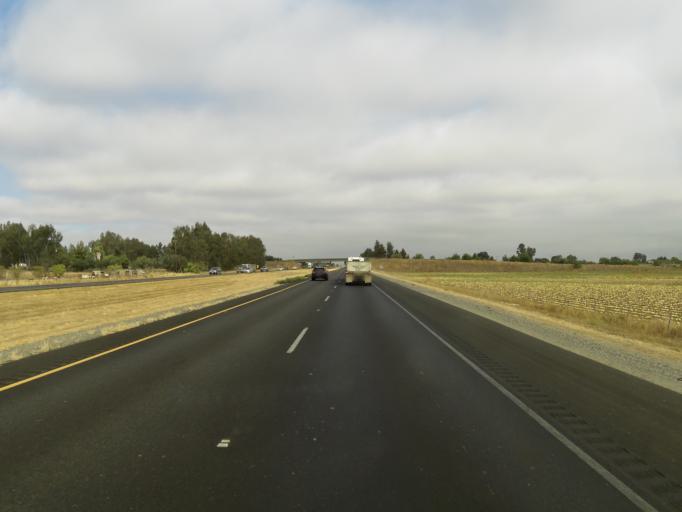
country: US
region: California
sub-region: Yolo County
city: Dunnigan
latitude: 38.9078
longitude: -121.9883
